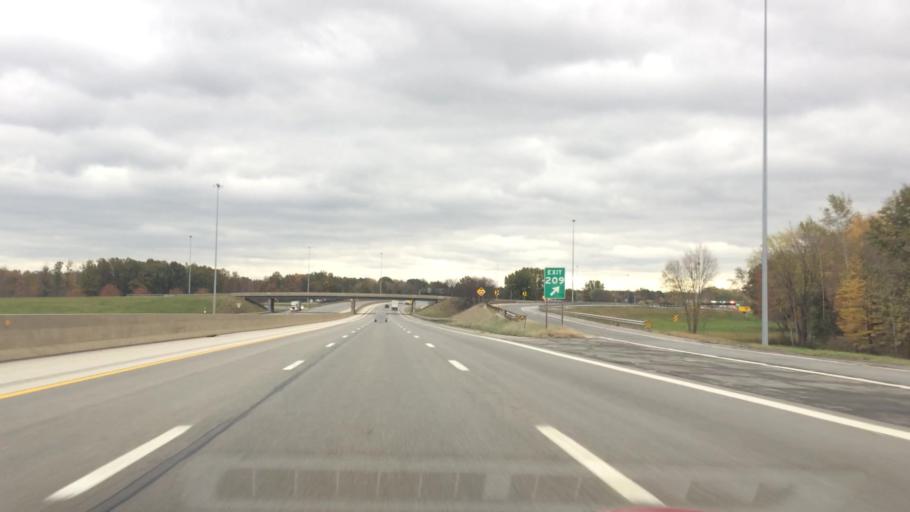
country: US
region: Ohio
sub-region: Trumbull County
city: Newton Falls
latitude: 41.2200
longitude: -80.9567
